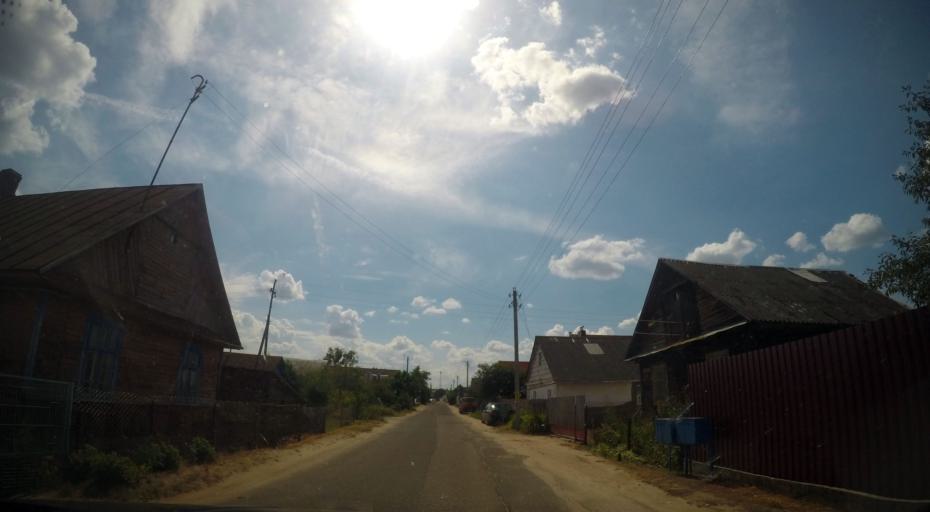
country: BY
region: Grodnenskaya
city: Hrodna
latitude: 53.6271
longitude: 23.8400
